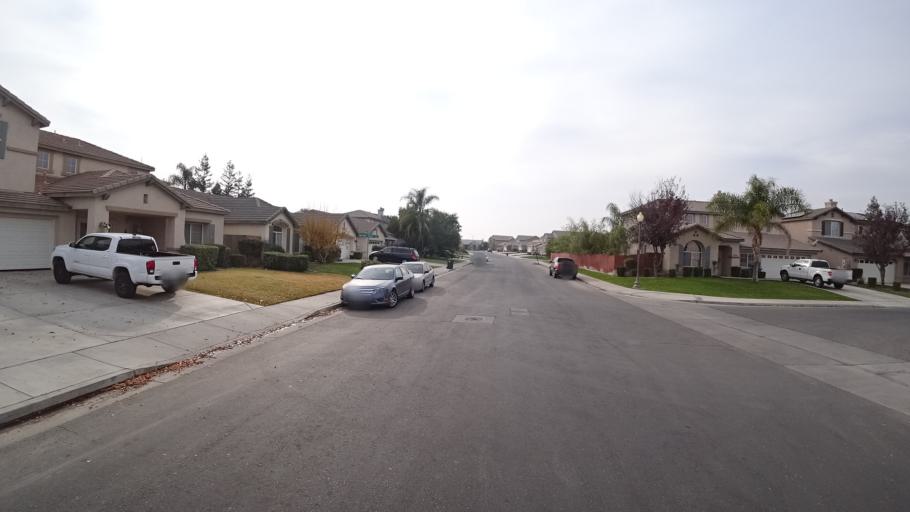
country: US
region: California
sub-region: Kern County
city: Rosedale
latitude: 35.3429
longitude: -119.1361
